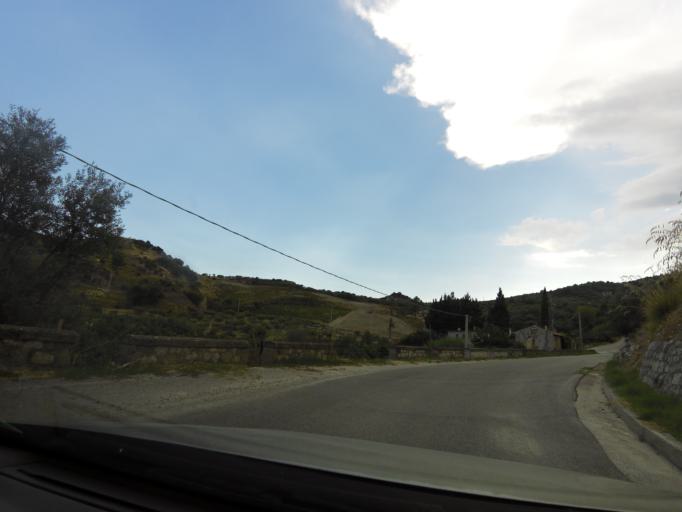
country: IT
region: Calabria
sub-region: Provincia di Reggio Calabria
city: Stilo
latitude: 38.4624
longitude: 16.4953
